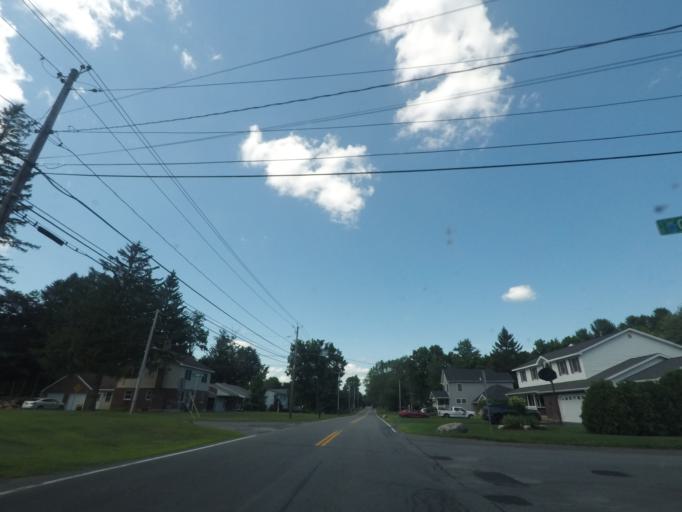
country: US
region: New York
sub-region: Schenectady County
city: Rotterdam
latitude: 42.7607
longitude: -73.9612
